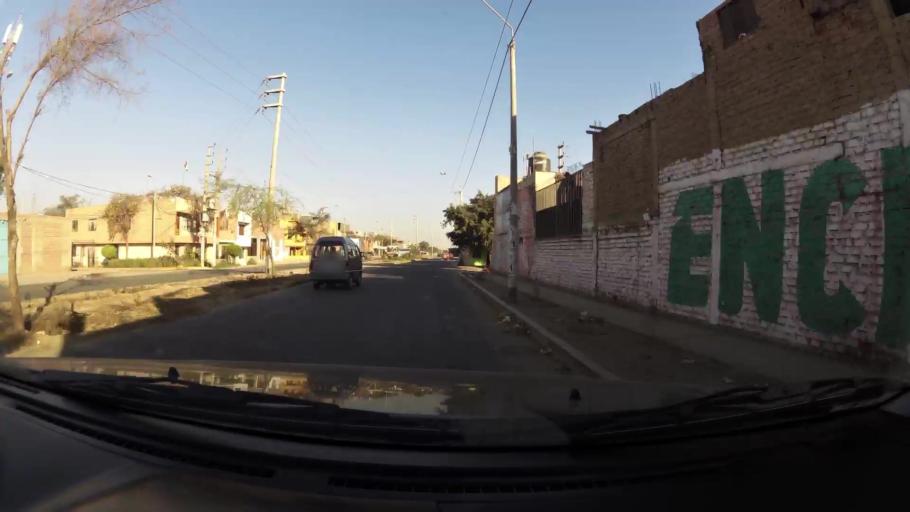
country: PE
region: Ica
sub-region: Provincia de Ica
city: Ica
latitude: -14.0683
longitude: -75.7187
